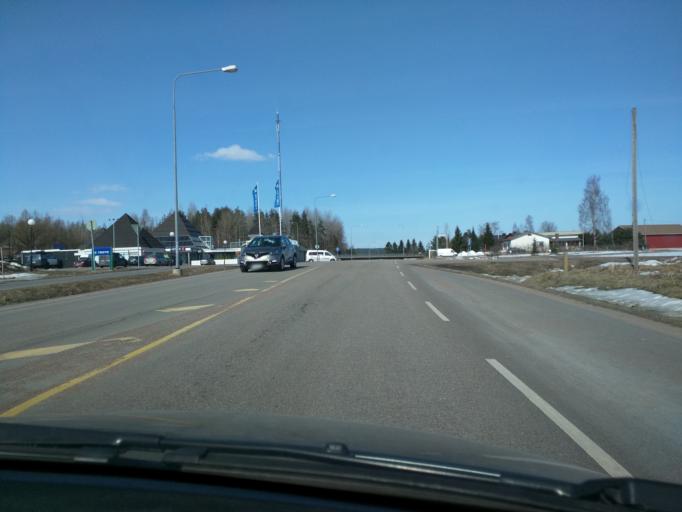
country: FI
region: Kymenlaakso
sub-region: Kouvola
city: Elimaeki
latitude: 60.7295
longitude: 26.4329
